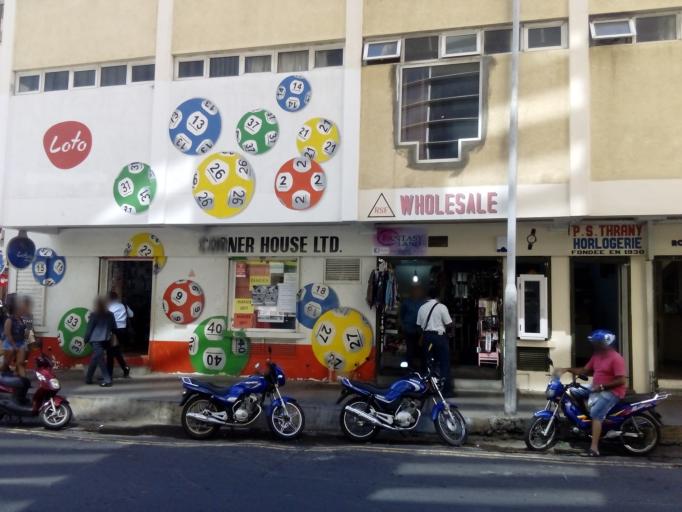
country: MU
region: Port Louis
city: Port Louis
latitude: -20.1618
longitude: 57.5036
